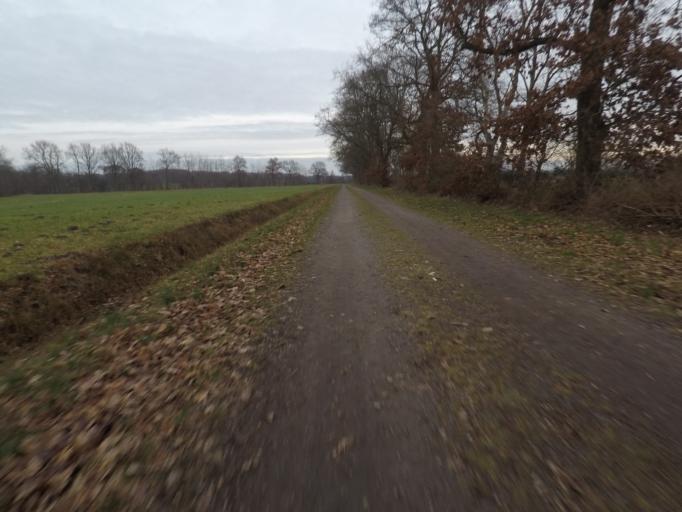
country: DE
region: Lower Saxony
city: Langen
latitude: 53.6074
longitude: 8.6216
